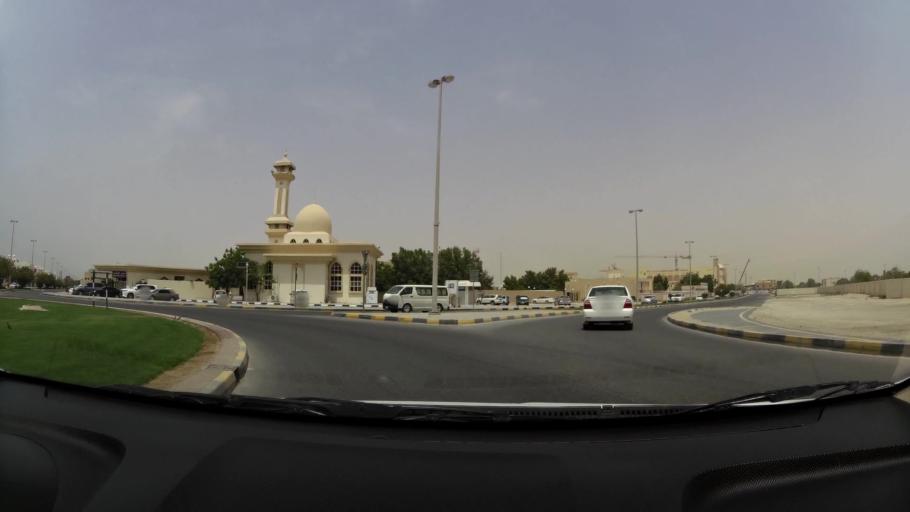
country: AE
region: Ash Shariqah
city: Sharjah
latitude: 25.3497
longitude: 55.4053
